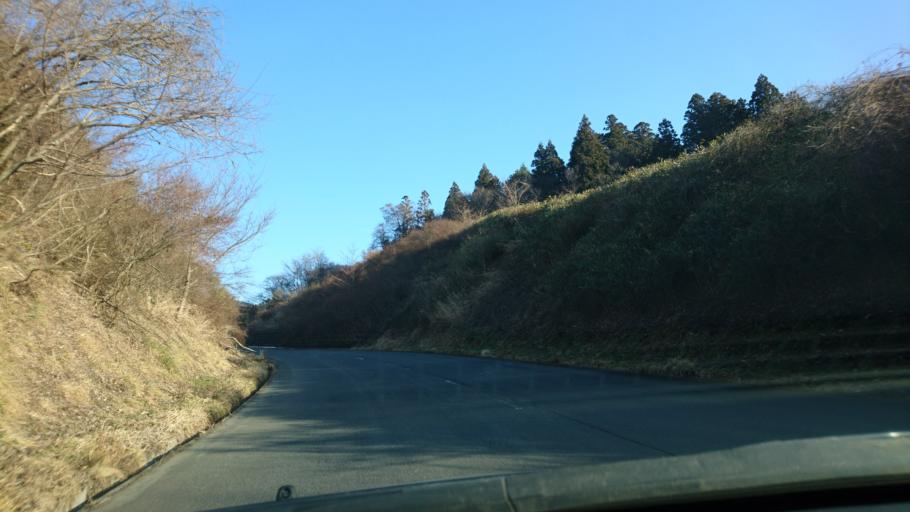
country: JP
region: Iwate
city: Ichinoseki
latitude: 38.8382
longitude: 141.3727
